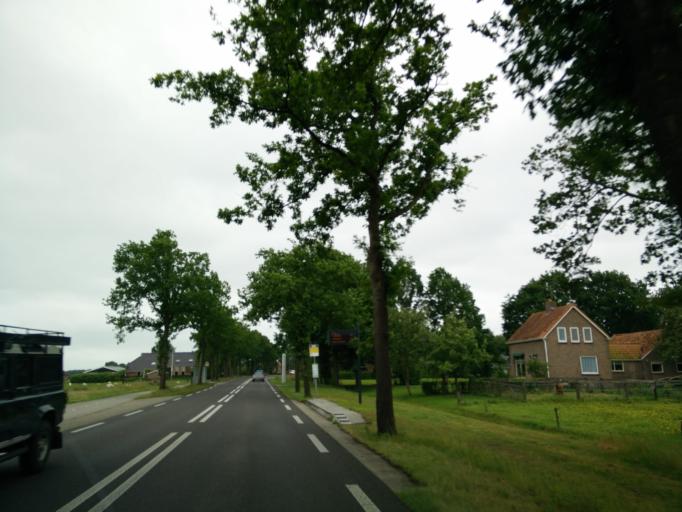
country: NL
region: Groningen
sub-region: Gemeente Groningen
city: Groningen
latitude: 53.1634
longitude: 6.4962
